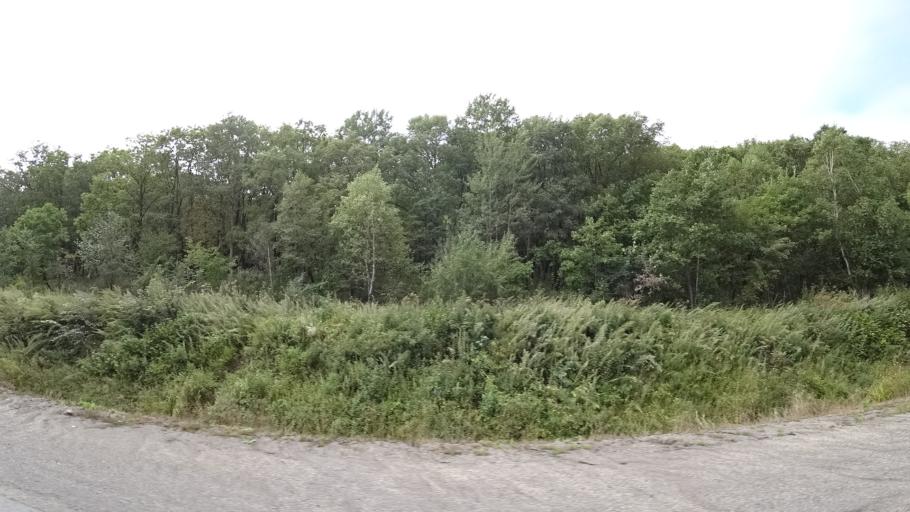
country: RU
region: Primorskiy
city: Lyalichi
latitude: 44.1022
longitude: 132.4239
